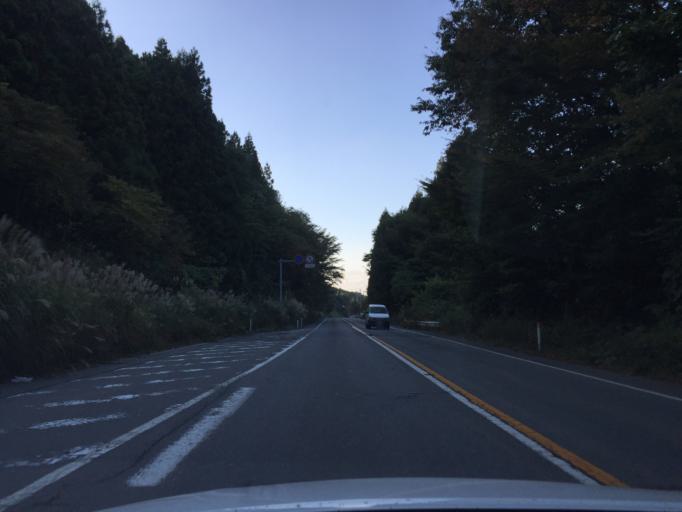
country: JP
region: Fukushima
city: Ishikawa
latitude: 37.1711
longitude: 140.6539
